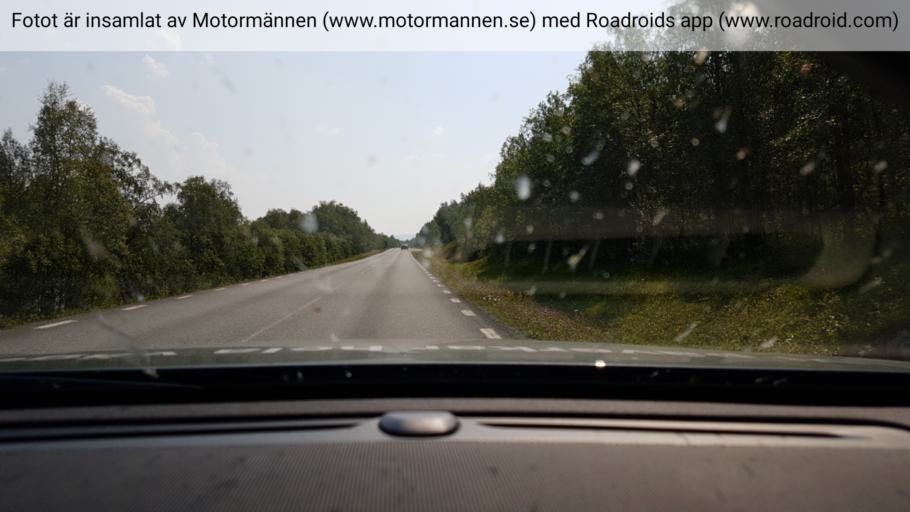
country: NO
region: Nordland
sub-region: Rana
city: Mo i Rana
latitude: 65.7239
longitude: 15.1835
